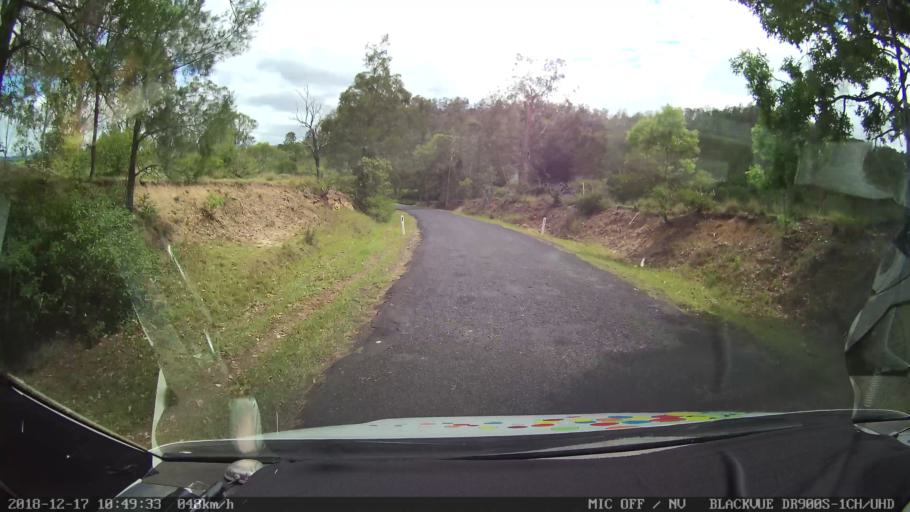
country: AU
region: New South Wales
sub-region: Clarence Valley
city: Gordon
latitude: -28.8650
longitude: 152.5738
